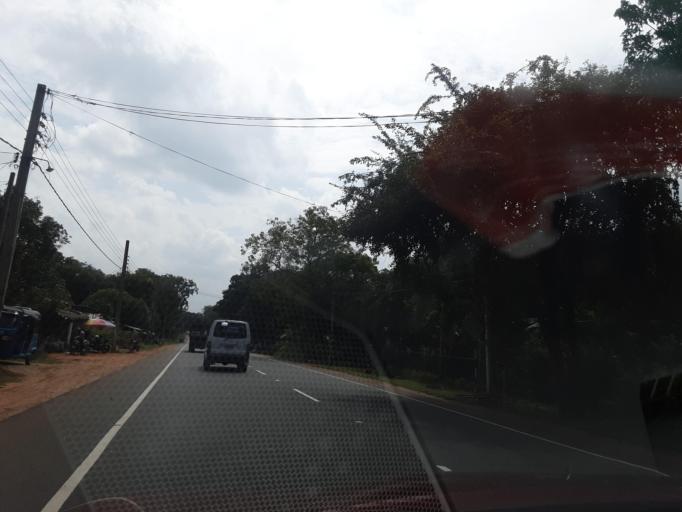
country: LK
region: North Central
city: Anuradhapura
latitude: 8.4886
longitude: 80.5110
